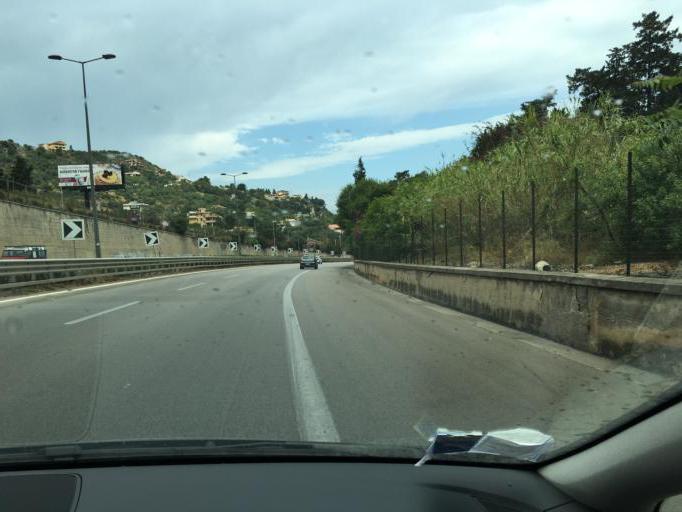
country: IT
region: Sicily
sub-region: Palermo
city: Isola delle Femmine
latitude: 38.1875
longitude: 13.2849
